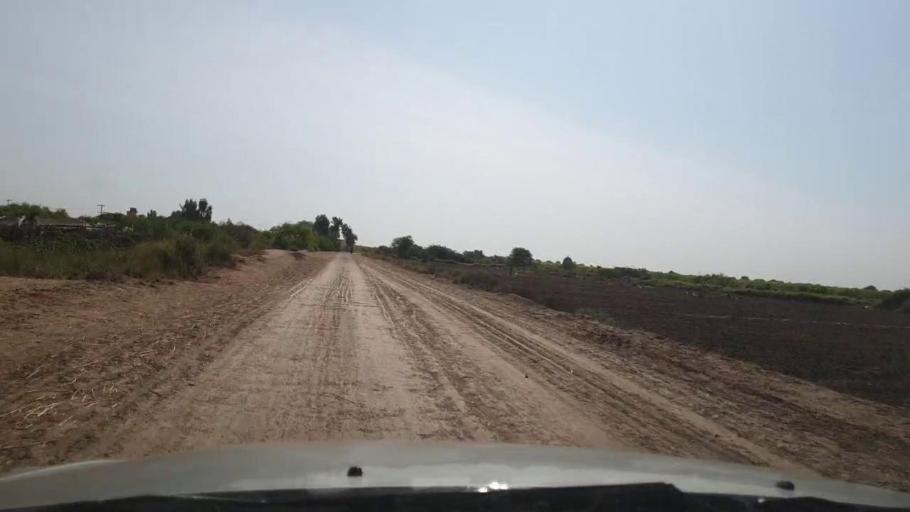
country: PK
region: Sindh
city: Bulri
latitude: 25.0032
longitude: 68.3199
